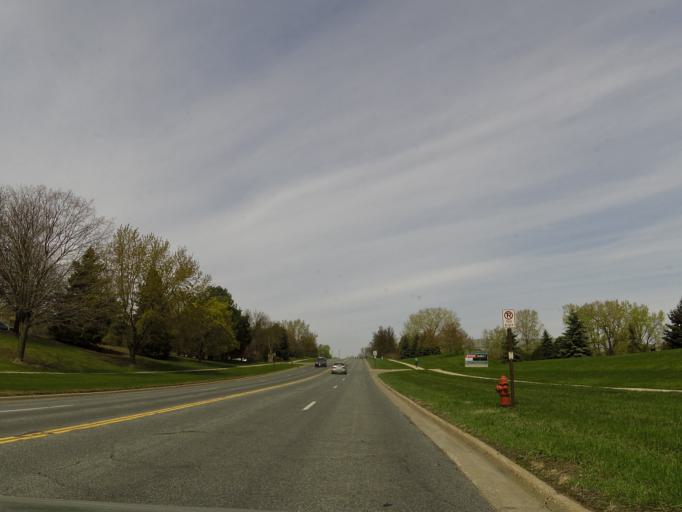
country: US
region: Minnesota
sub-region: Scott County
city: Savage
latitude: 44.8088
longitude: -93.3685
